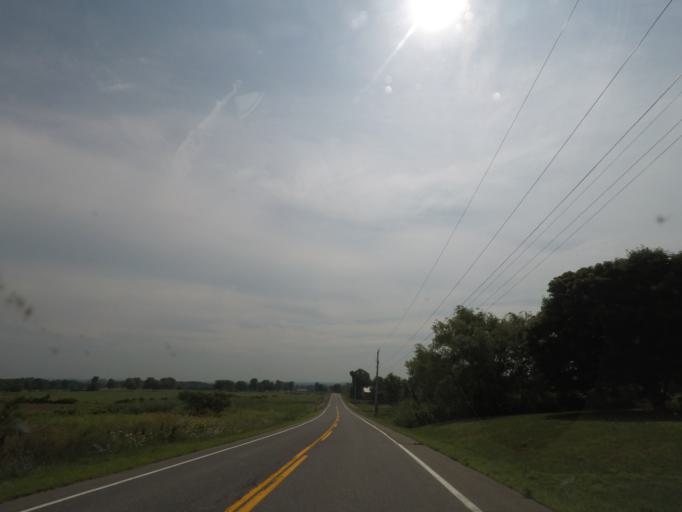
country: US
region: New York
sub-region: Saratoga County
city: Mechanicville
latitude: 42.8891
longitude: -73.7159
